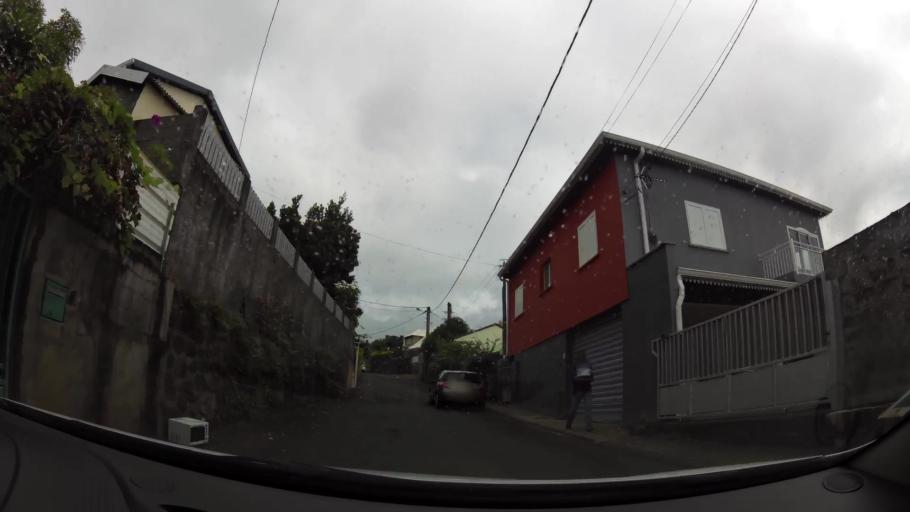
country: RE
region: Reunion
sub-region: Reunion
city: Sainte-Marie
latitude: -20.8992
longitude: 55.5483
